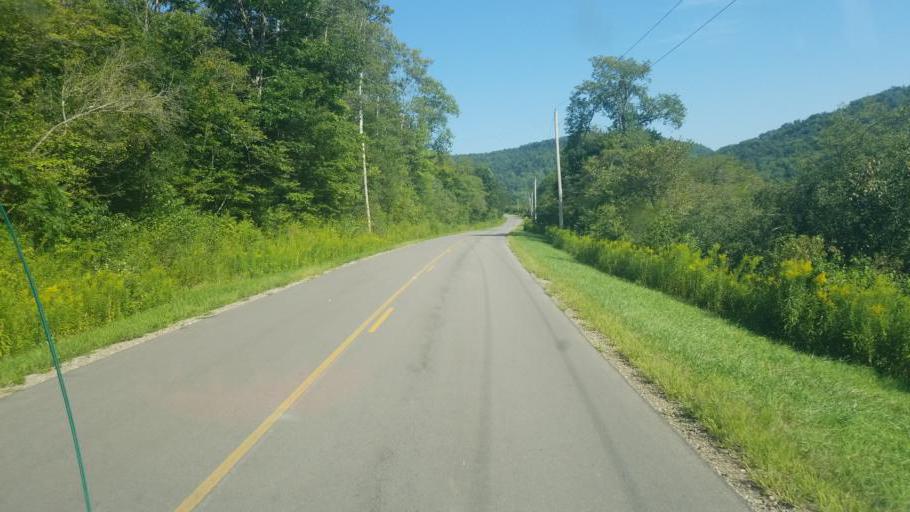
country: US
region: New York
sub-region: Allegany County
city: Bolivar
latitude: 42.0116
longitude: -78.0481
